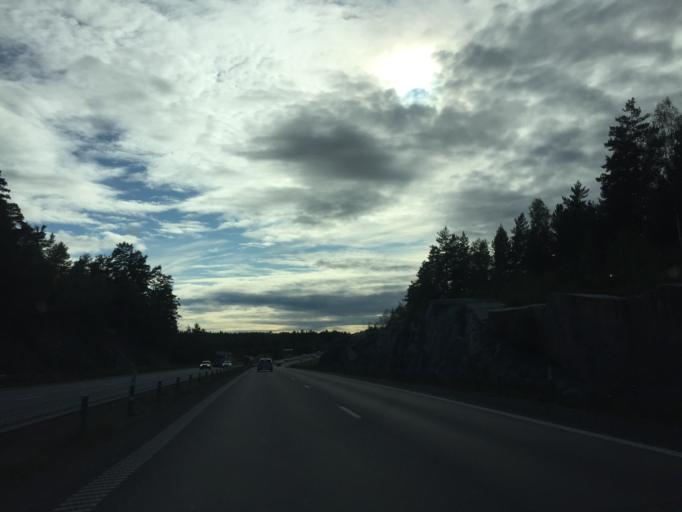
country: SE
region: Vaestmanland
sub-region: Vasteras
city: Skultuna
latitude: 59.5962
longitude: 16.4306
